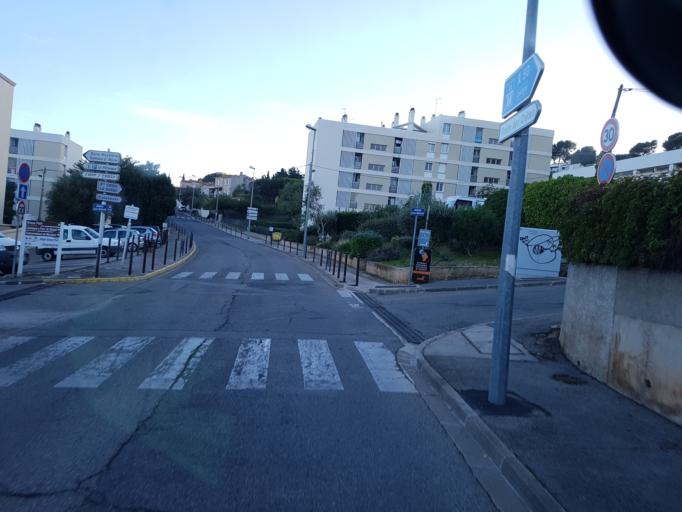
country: FR
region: Provence-Alpes-Cote d'Azur
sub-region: Departement des Bouches-du-Rhone
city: La Ciotat
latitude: 43.1759
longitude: 5.5977
